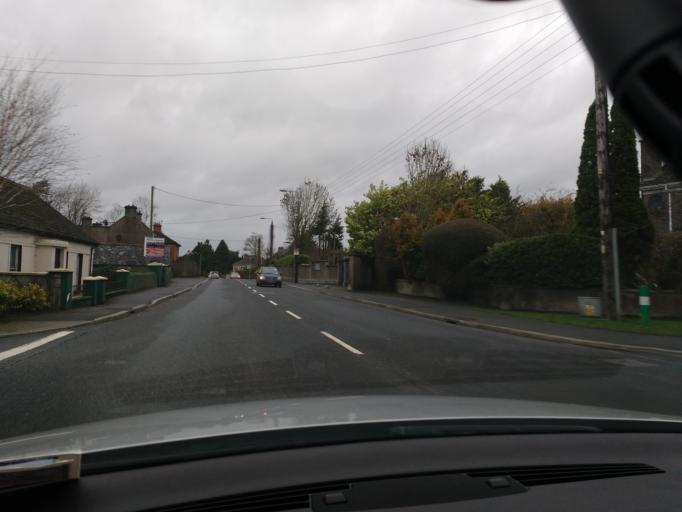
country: IE
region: Munster
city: Thurles
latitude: 52.6789
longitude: -7.7942
